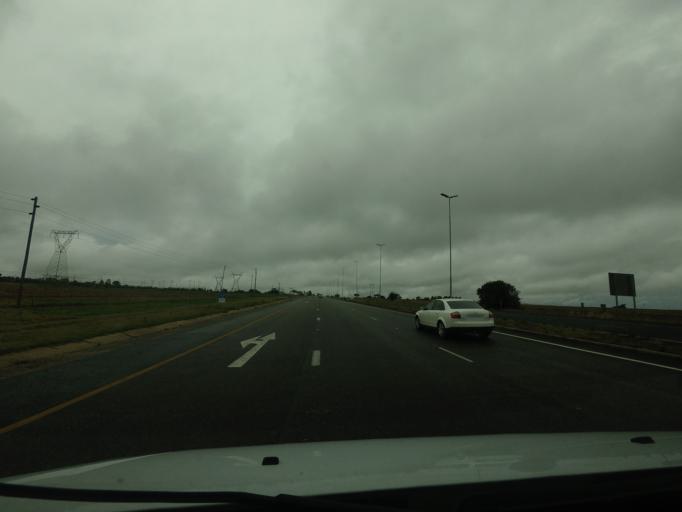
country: ZA
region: Mpumalanga
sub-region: Nkangala District Municipality
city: Belfast
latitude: -25.8151
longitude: 29.8884
